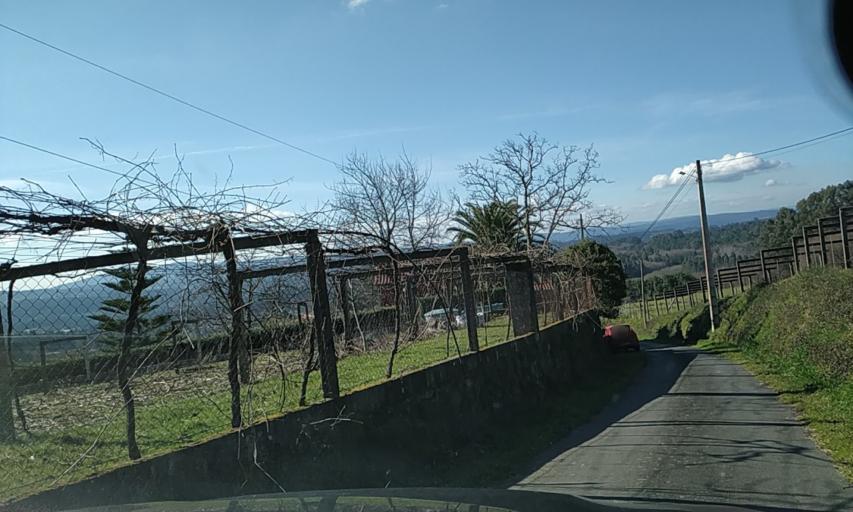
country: ES
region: Galicia
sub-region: Provincia da Coruna
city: Ribeira
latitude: 42.7070
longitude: -8.4268
